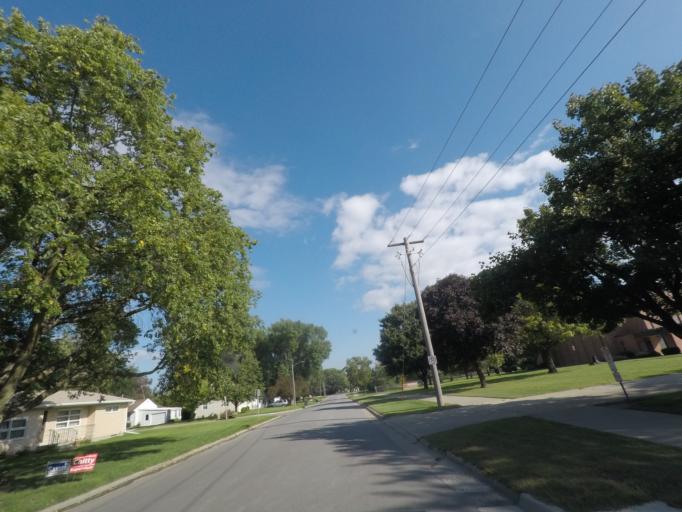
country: US
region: Iowa
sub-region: Story County
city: Nevada
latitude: 42.0166
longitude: -93.4447
